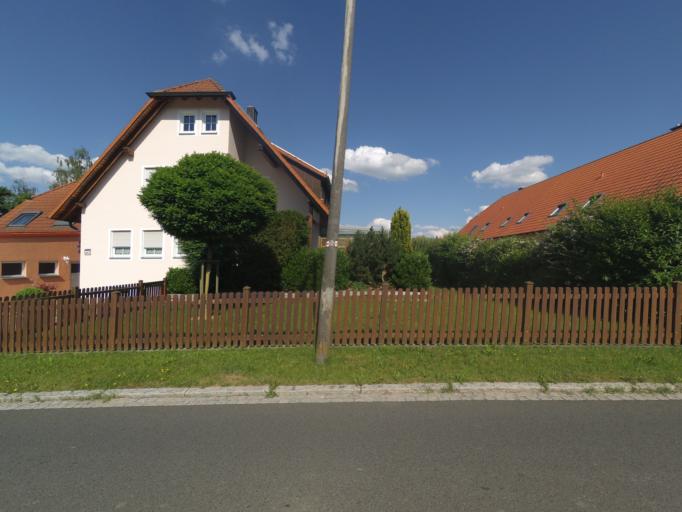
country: DE
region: Bavaria
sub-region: Regierungsbezirk Mittelfranken
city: Wilhermsdorf
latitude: 49.5173
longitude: 10.7201
